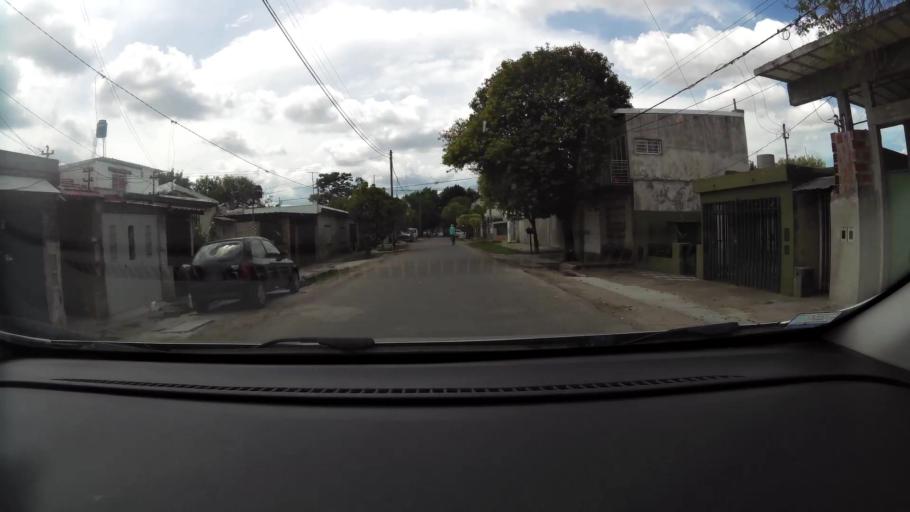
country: AR
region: Santa Fe
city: Gobernador Galvez
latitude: -33.0134
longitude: -60.6466
